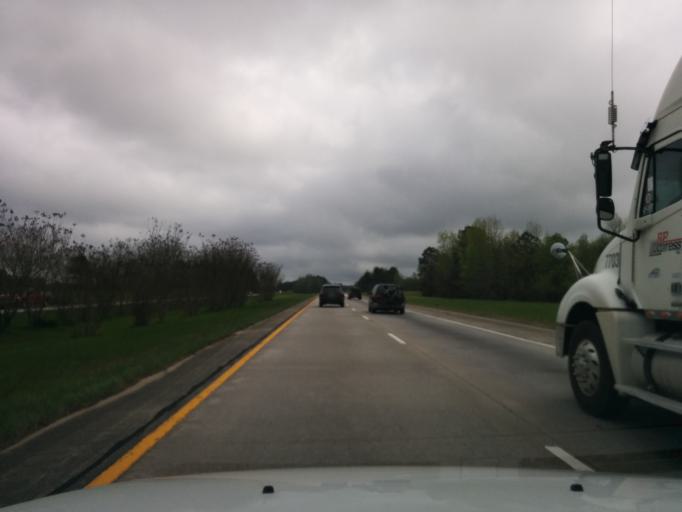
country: US
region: Georgia
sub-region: Candler County
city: Metter
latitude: 32.3808
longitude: -82.2148
